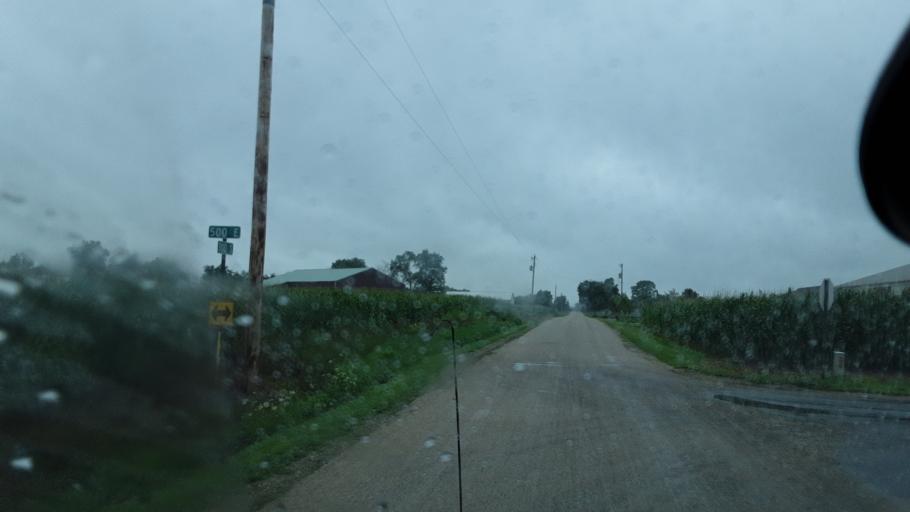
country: US
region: Indiana
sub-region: Adams County
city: Berne
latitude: 40.7029
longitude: -84.8407
